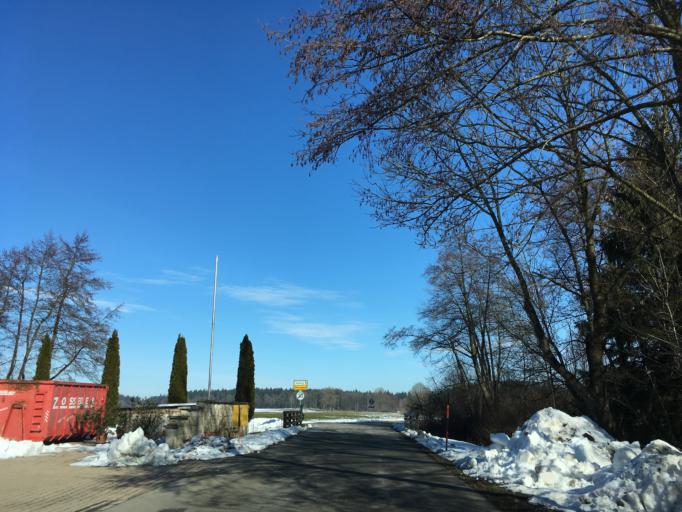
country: DE
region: Bavaria
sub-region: Upper Bavaria
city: Edling
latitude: 48.0730
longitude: 12.1594
